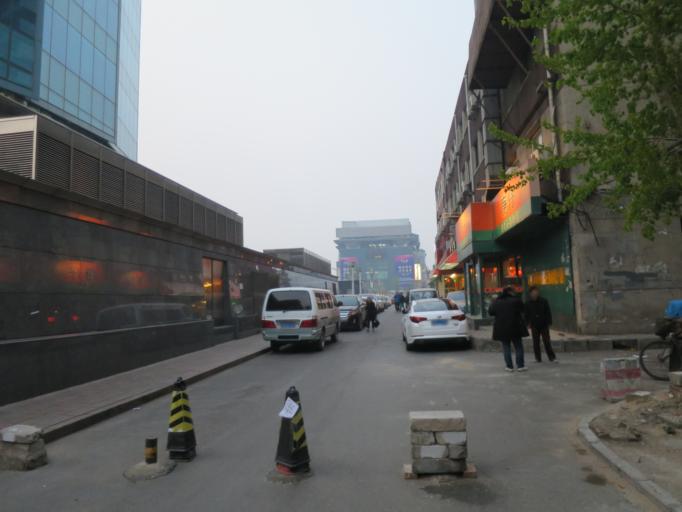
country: CN
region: Beijing
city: Chaowai
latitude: 39.9059
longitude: 116.4435
